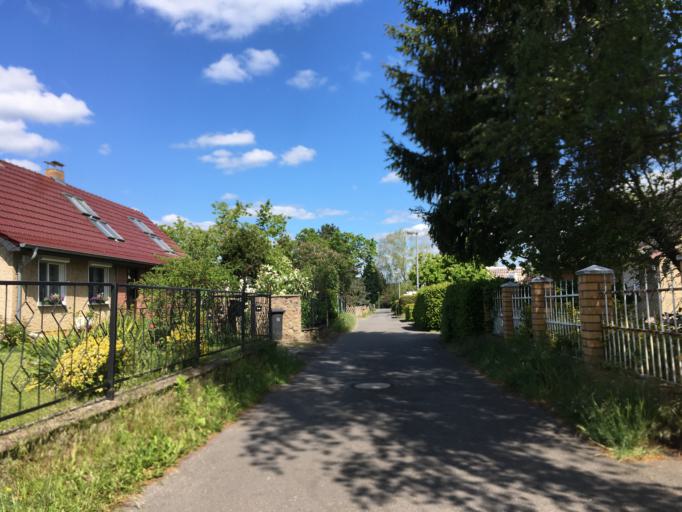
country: DE
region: Berlin
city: Blankenfelde
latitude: 52.6288
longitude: 13.3862
